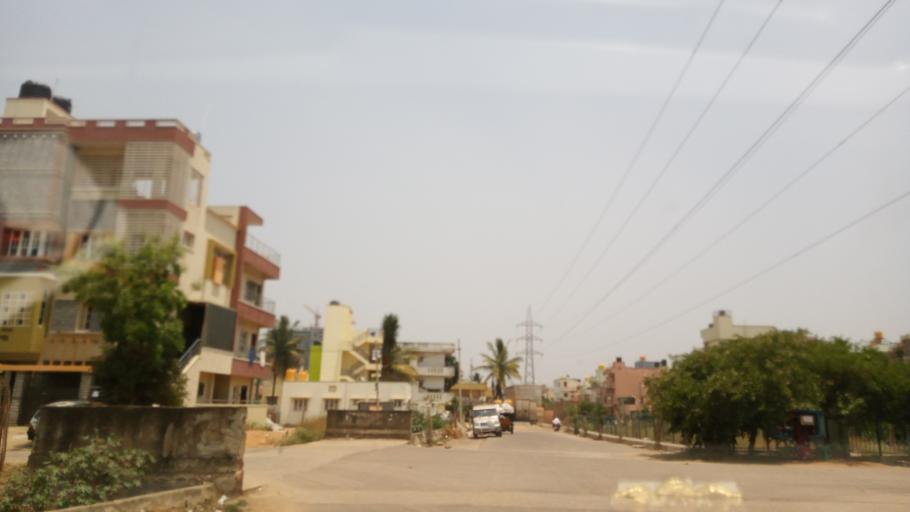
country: IN
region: Karnataka
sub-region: Bangalore Urban
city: Yelahanka
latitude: 13.0396
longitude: 77.5024
